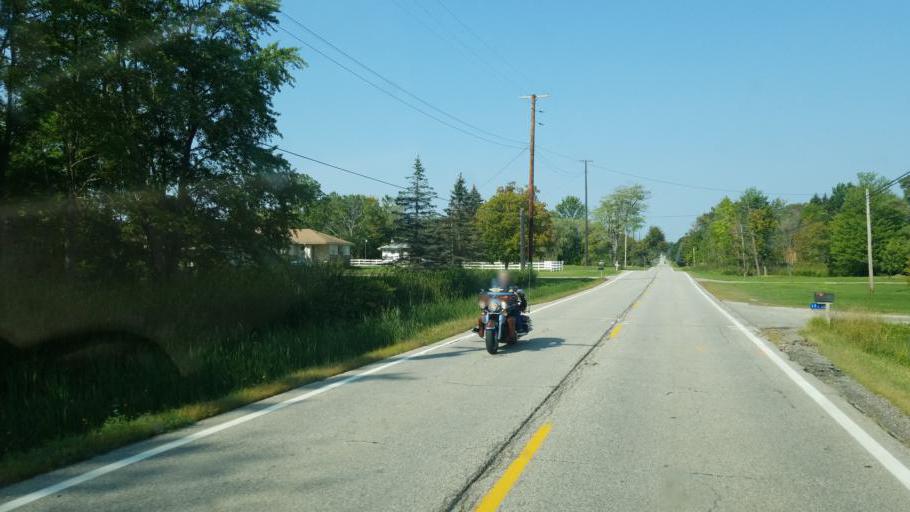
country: US
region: Ohio
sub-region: Geauga County
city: Chardon
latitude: 41.6073
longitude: -81.0265
